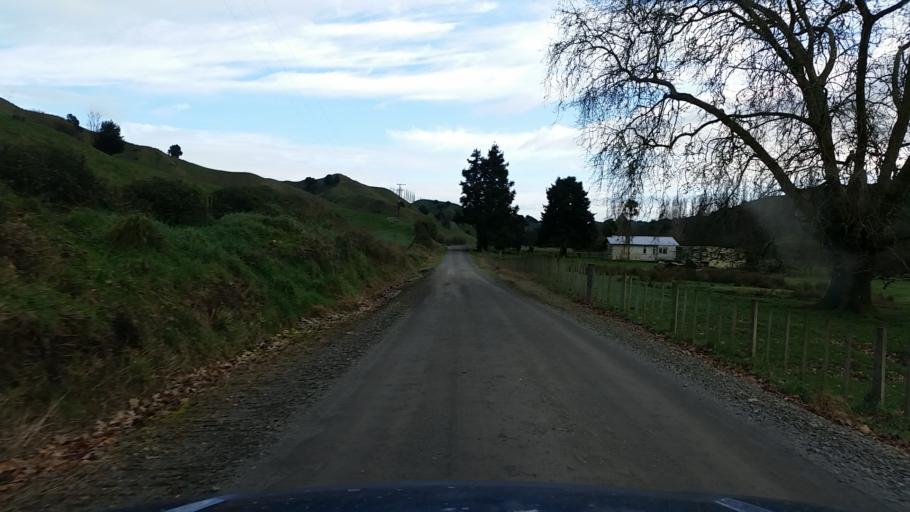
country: NZ
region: Taranaki
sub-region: New Plymouth District
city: Waitara
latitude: -39.0863
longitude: 174.8309
